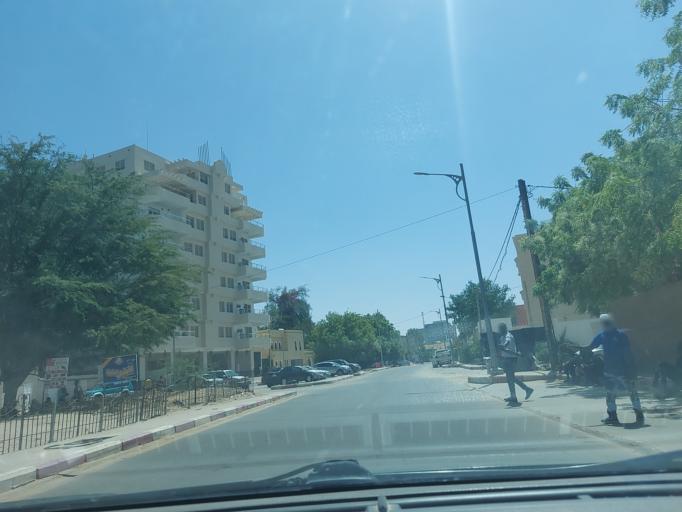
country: MR
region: Nouakchott
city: Nouakchott
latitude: 18.0952
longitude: -15.9803
